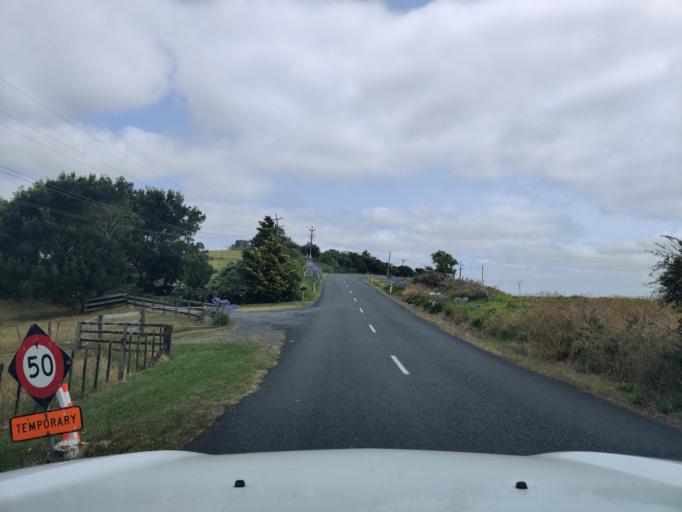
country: NZ
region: Waikato
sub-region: Waikato District
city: Te Kauwhata
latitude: -37.5210
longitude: 175.1770
